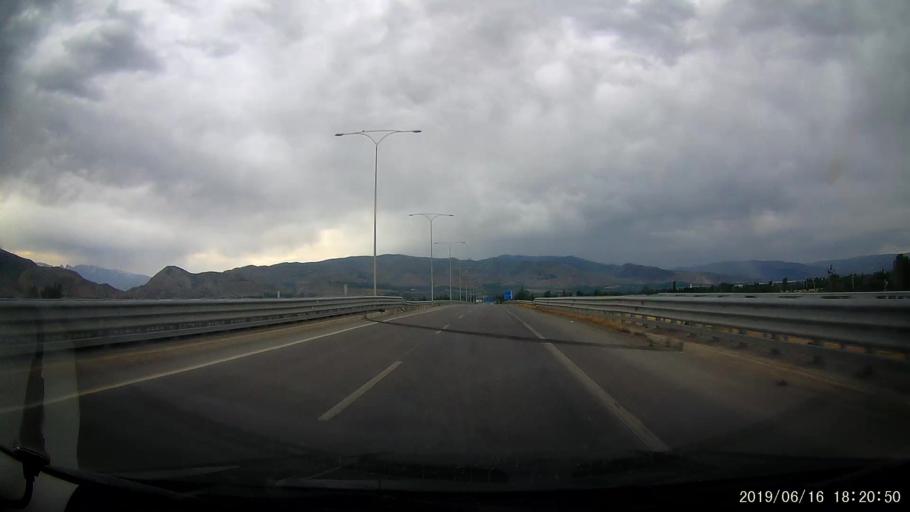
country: TR
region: Erzincan
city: Erzincan
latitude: 39.7204
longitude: 39.4590
